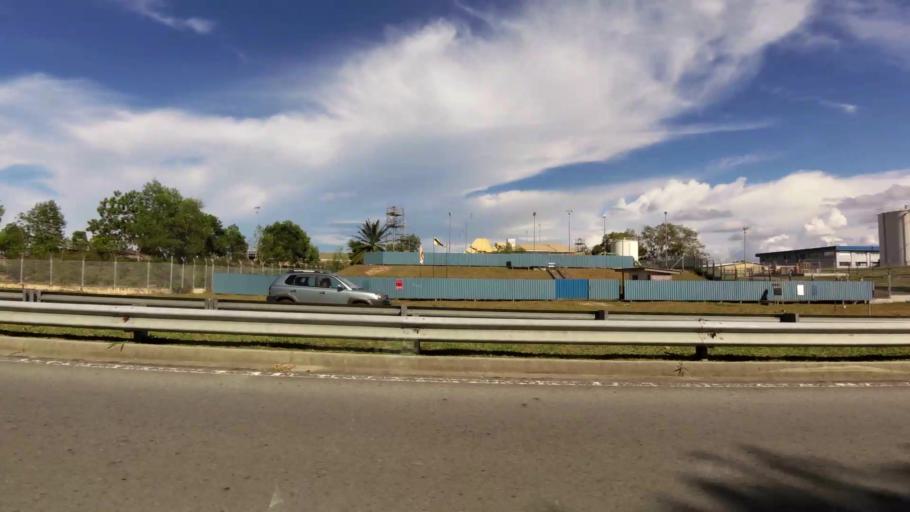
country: BN
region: Brunei and Muara
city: Bandar Seri Begawan
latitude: 4.9722
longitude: 114.9286
